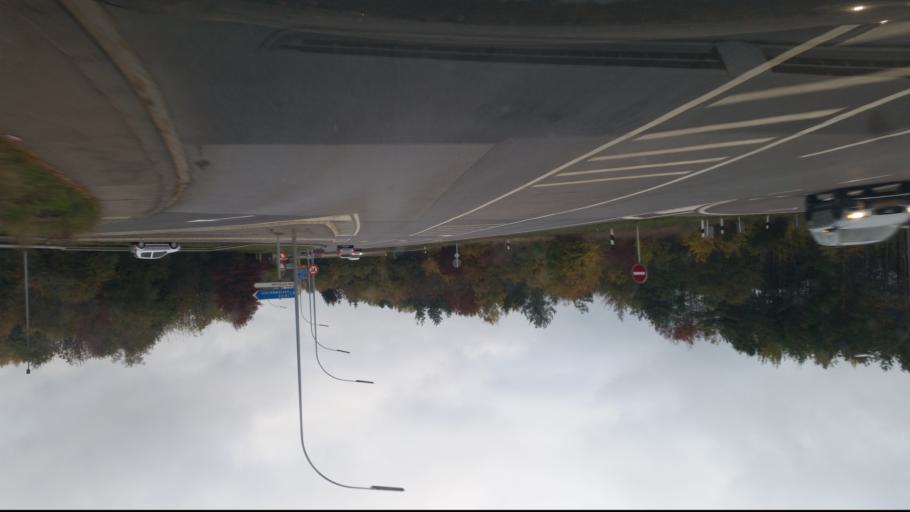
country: LU
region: Luxembourg
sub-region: Canton de Luxembourg
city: Sandweiler
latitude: 49.6411
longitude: 6.2171
